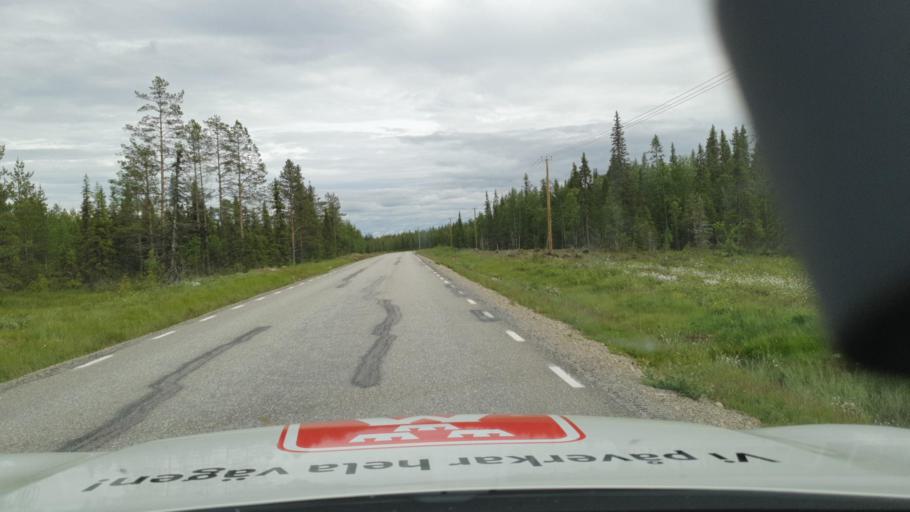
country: SE
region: Vaesterbotten
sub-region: Lycksele Kommun
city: Soderfors
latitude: 64.3761
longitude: 18.0409
